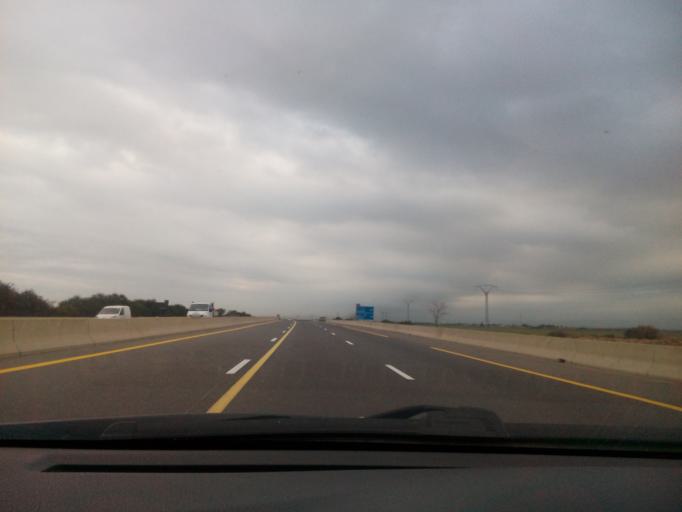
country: DZ
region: Relizane
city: Relizane
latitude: 35.7909
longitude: 0.4744
